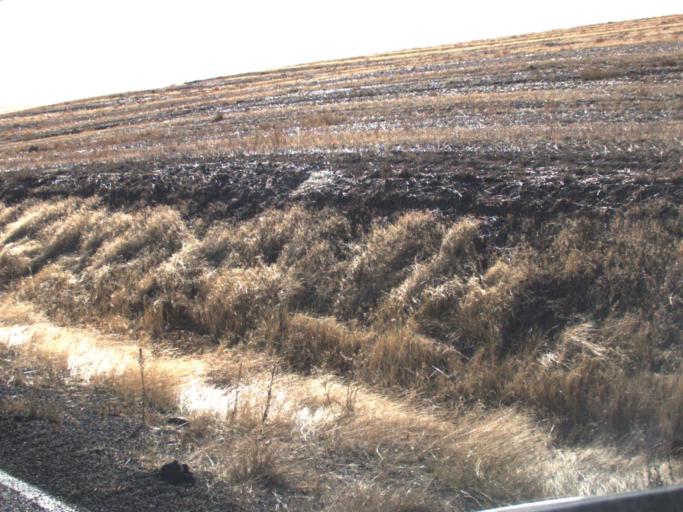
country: US
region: Washington
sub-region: Walla Walla County
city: Walla Walla
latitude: 46.1094
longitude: -118.3734
